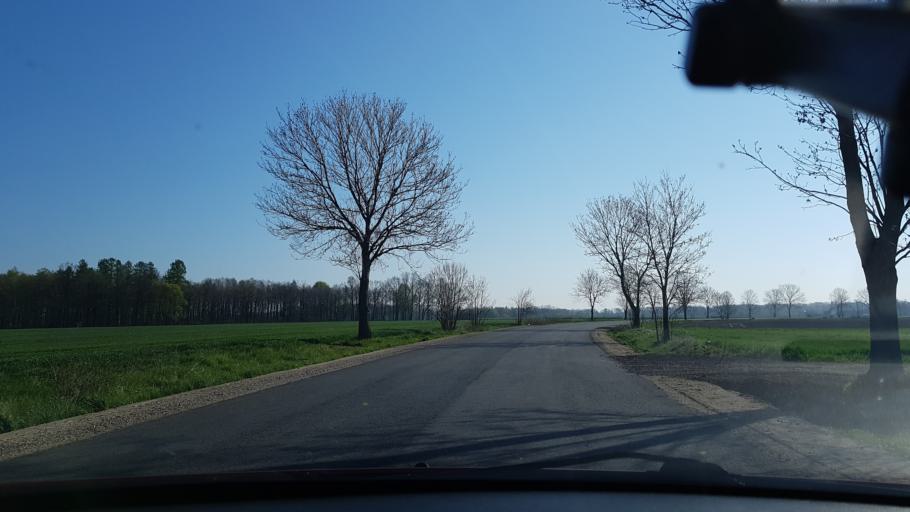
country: CZ
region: Olomoucky
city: Vidnava
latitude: 50.4260
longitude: 17.2390
